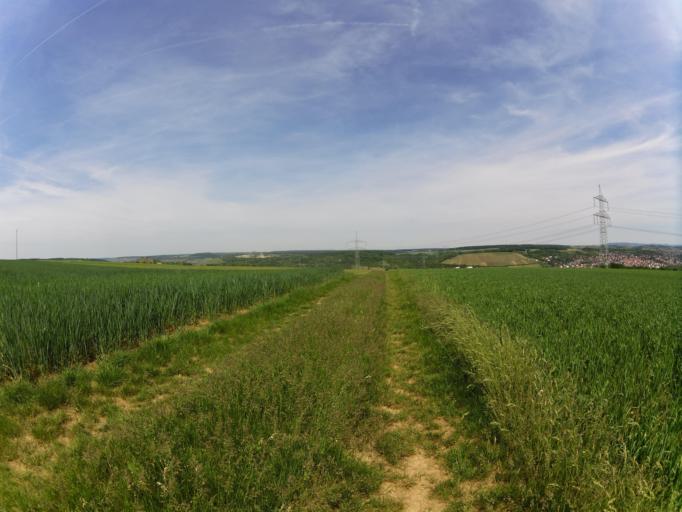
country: DE
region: Bavaria
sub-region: Regierungsbezirk Unterfranken
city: Ochsenfurt
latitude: 49.6659
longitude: 10.0325
